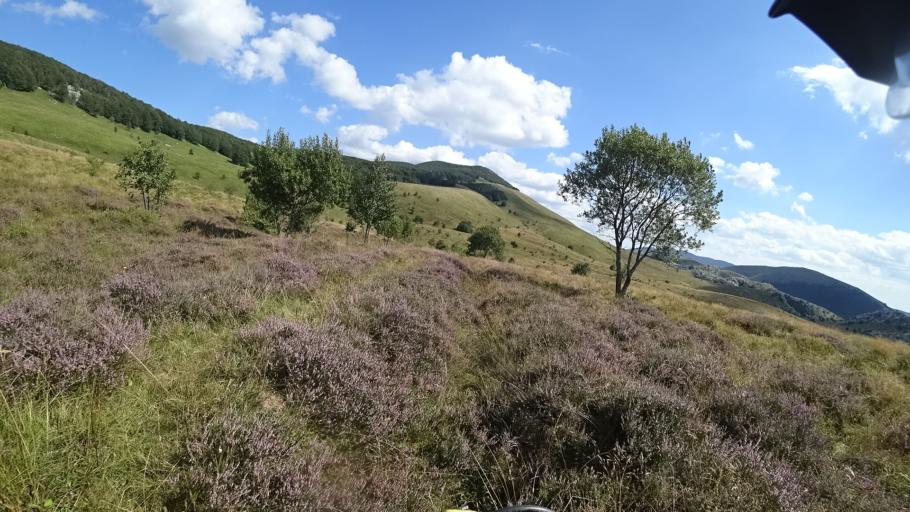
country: HR
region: Zadarska
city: Gracac
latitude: 44.4178
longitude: 15.9999
